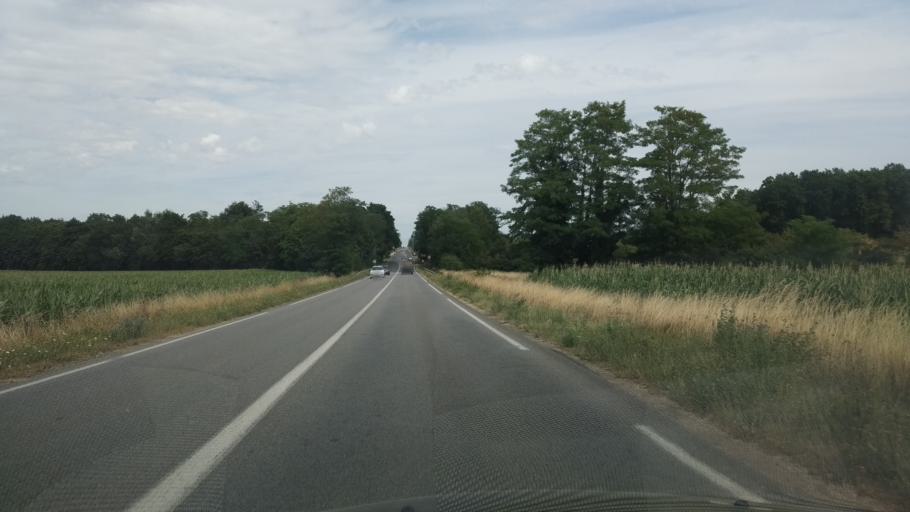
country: FR
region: Poitou-Charentes
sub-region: Departement de la Vienne
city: Mignaloux-Beauvoir
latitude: 46.5622
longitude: 0.4238
